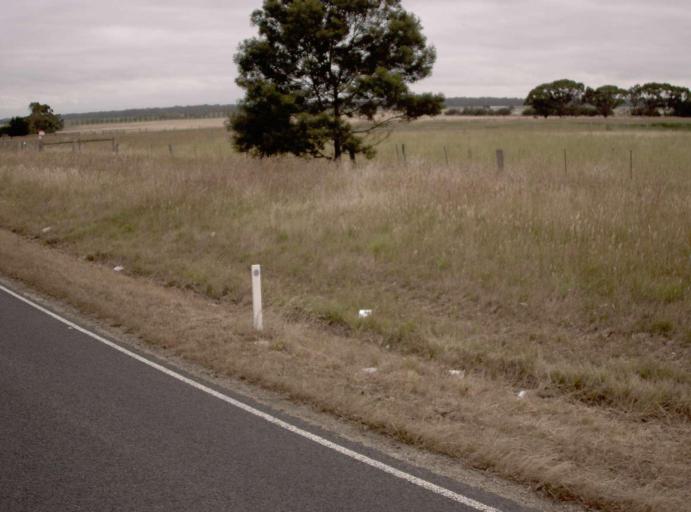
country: AU
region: Victoria
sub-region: Wellington
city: Sale
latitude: -38.0939
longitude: 146.9863
